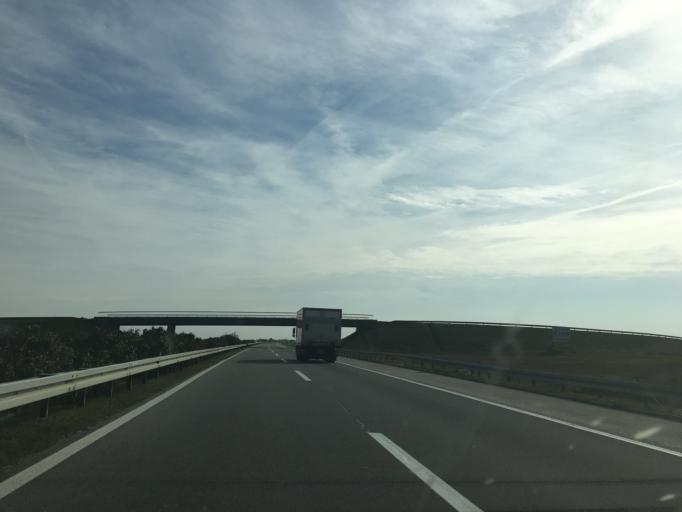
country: RS
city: Novi Karlovci
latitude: 45.0484
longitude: 20.1754
